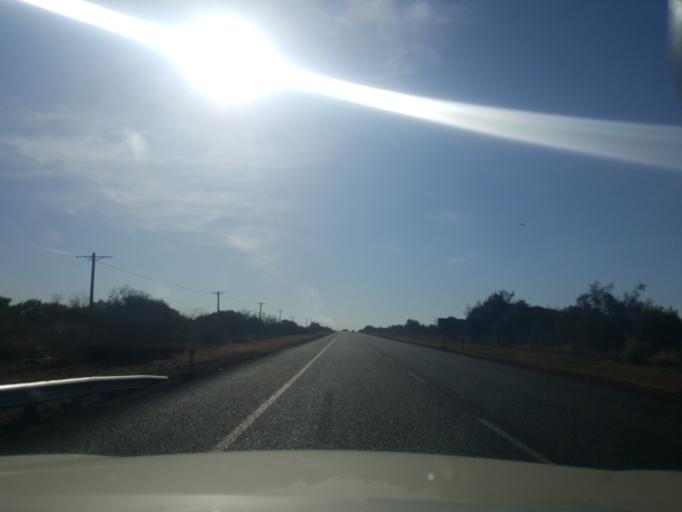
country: ZA
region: North-West
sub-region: Ngaka Modiri Molema District Municipality
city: Zeerust
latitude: -25.5148
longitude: 25.9981
